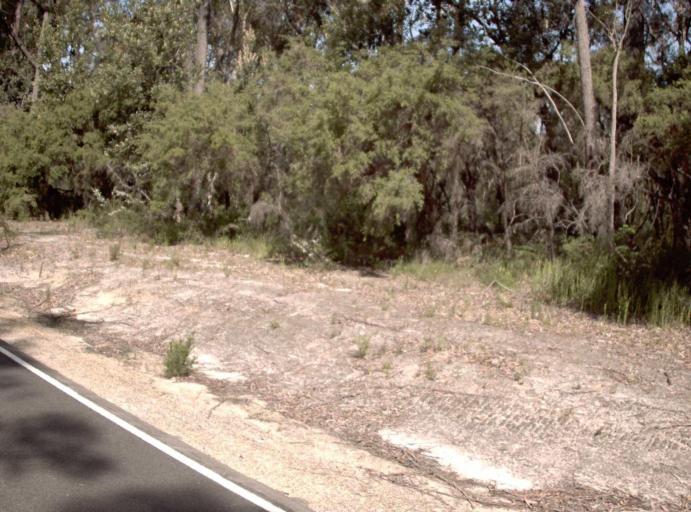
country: AU
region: New South Wales
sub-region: Bega Valley
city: Eden
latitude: -37.5447
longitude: 149.7036
